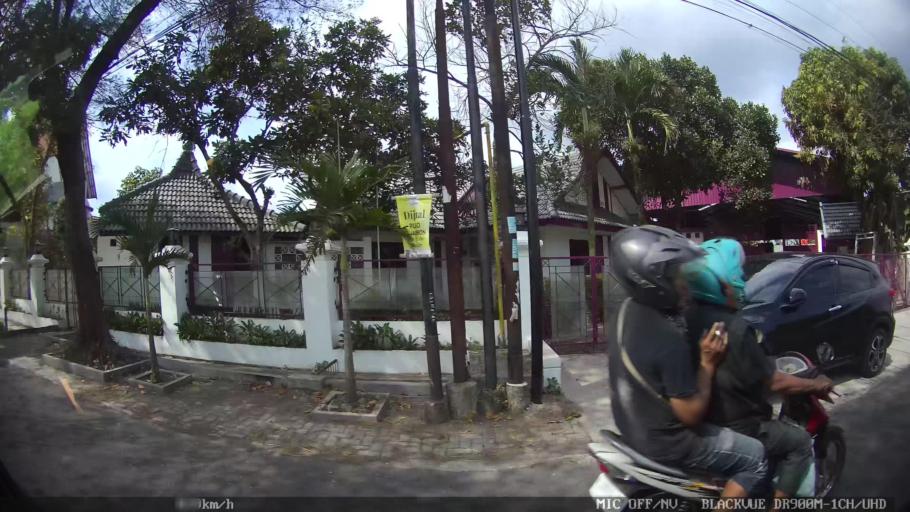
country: ID
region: Daerah Istimewa Yogyakarta
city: Yogyakarta
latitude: -7.7572
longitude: 110.3422
